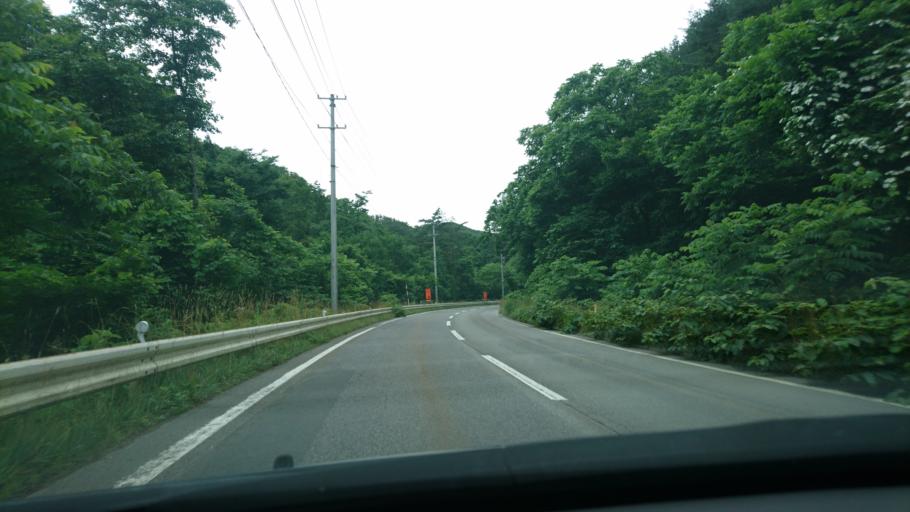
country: JP
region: Iwate
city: Miyako
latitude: 39.9755
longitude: 141.8595
